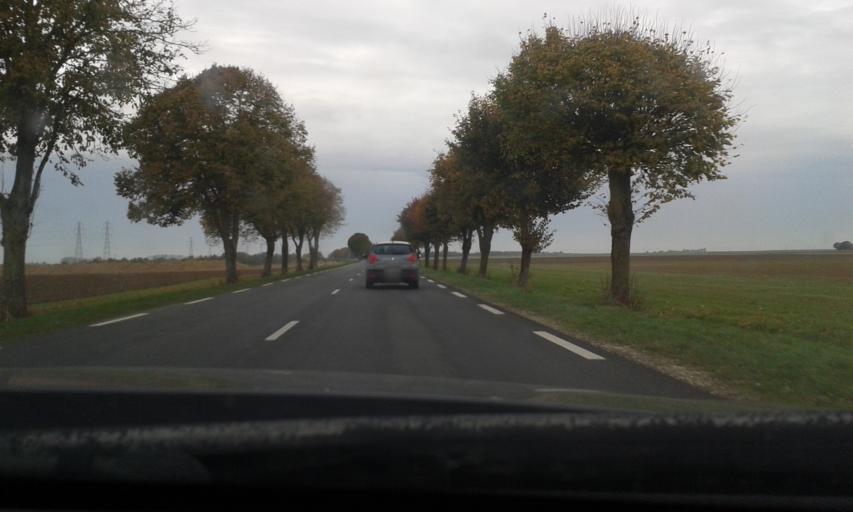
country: FR
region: Centre
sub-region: Departement du Loiret
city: Artenay
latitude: 48.1196
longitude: 1.8583
